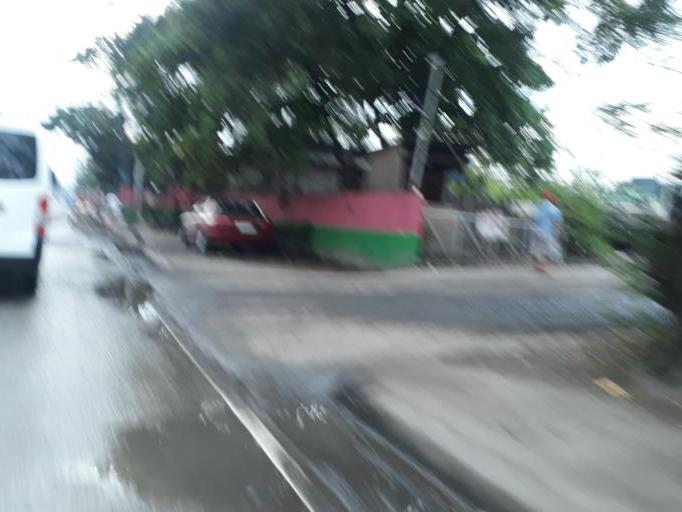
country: PH
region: Calabarzon
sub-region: Province of Rizal
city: Valenzuela
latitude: 14.6925
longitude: 120.9555
